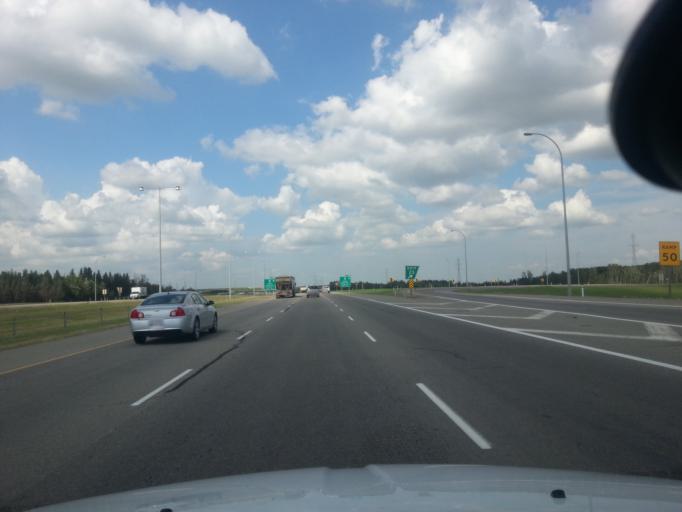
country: CA
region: Alberta
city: St. Albert
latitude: 53.5548
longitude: -113.6587
